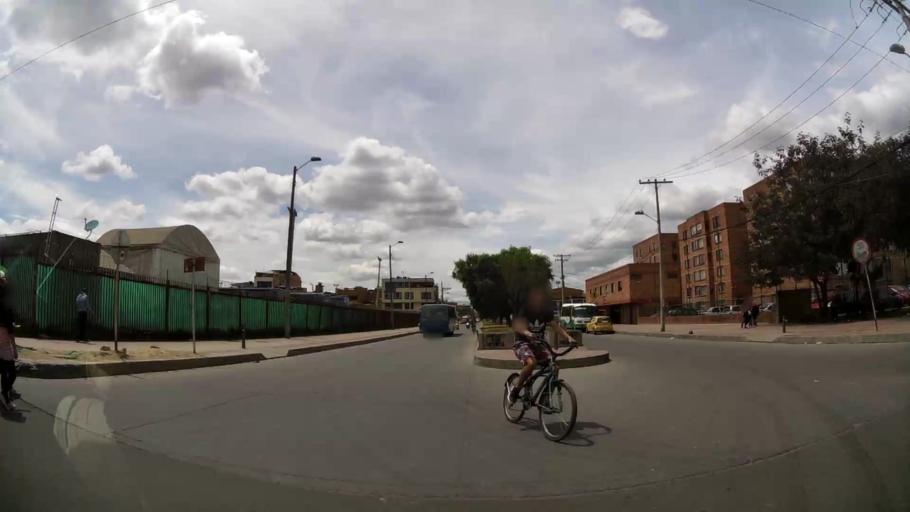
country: CO
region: Cundinamarca
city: Soacha
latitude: 4.6411
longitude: -74.1653
